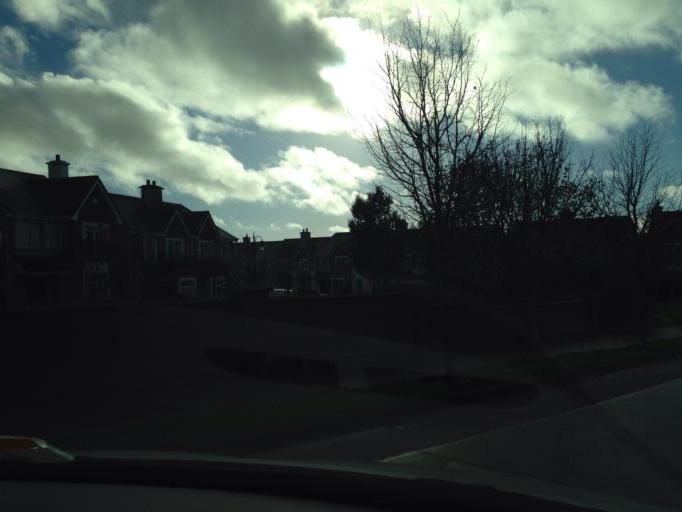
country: IE
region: Connaught
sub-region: County Galway
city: Oranmore
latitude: 53.2777
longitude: -8.9718
